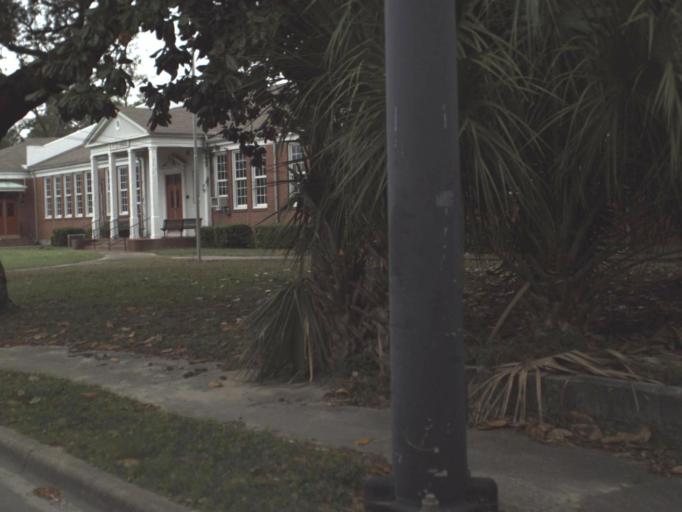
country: US
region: Florida
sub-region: Escambia County
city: Pensacola
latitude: 30.4238
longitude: -87.2032
